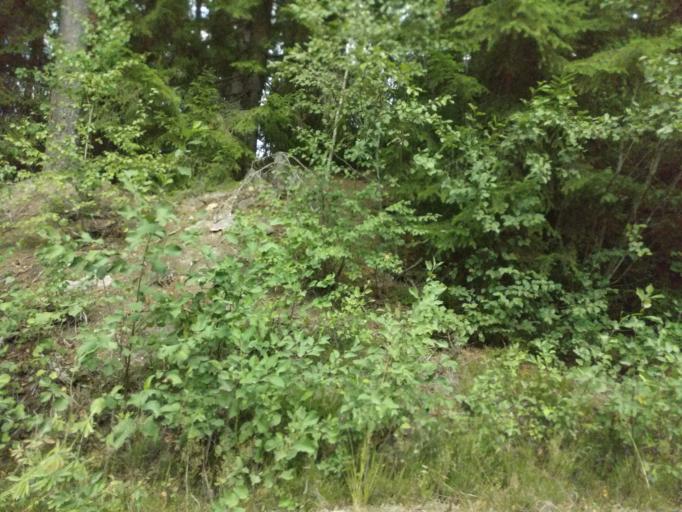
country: SE
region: Vaermland
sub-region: Hagfors Kommun
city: Hagfors
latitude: 60.0088
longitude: 13.6880
